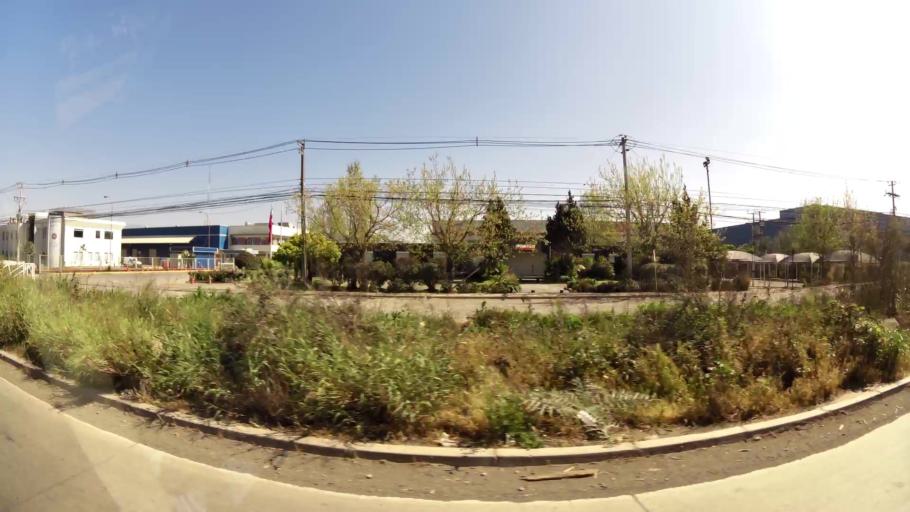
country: CL
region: Santiago Metropolitan
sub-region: Provincia de Chacabuco
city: Chicureo Abajo
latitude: -33.3169
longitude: -70.7305
